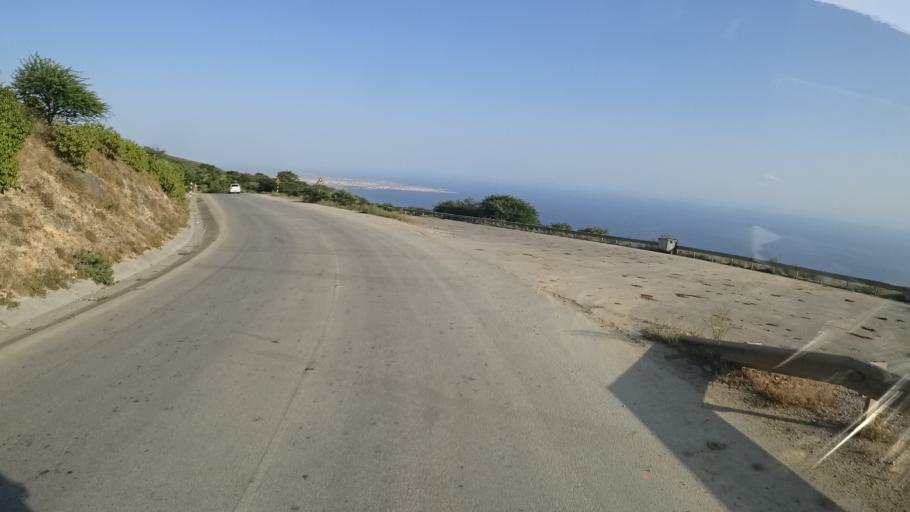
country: OM
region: Zufar
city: Salalah
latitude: 17.0576
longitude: 54.6101
